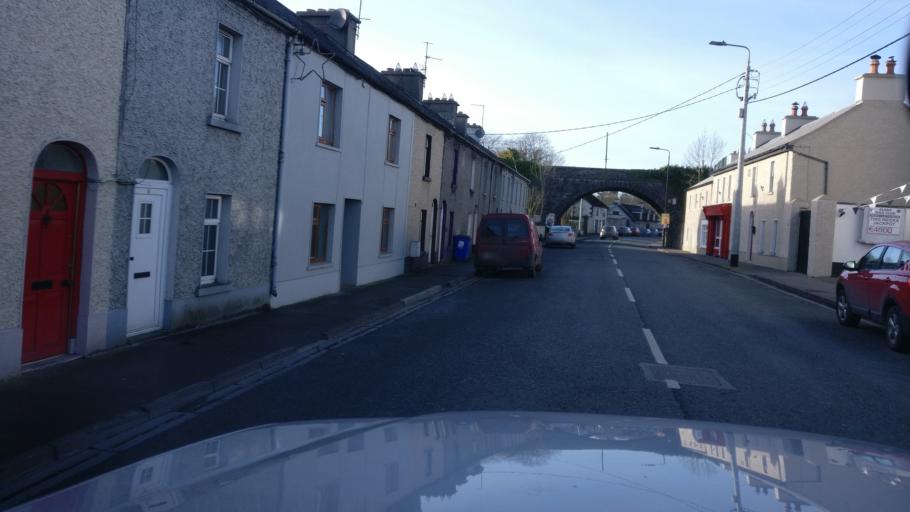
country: IE
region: Leinster
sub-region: Uibh Fhaili
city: Clara
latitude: 53.3414
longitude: -7.6103
